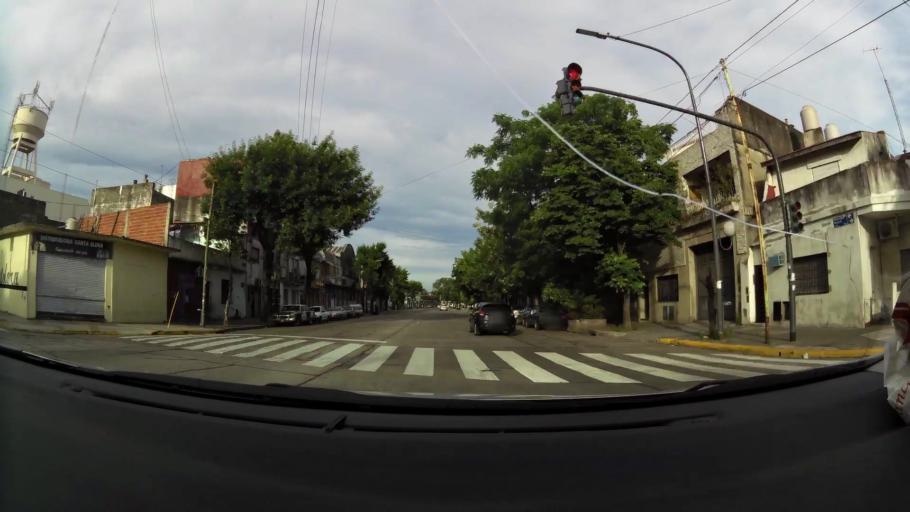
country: AR
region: Buenos Aires F.D.
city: Villa Lugano
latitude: -34.6463
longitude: -58.4349
